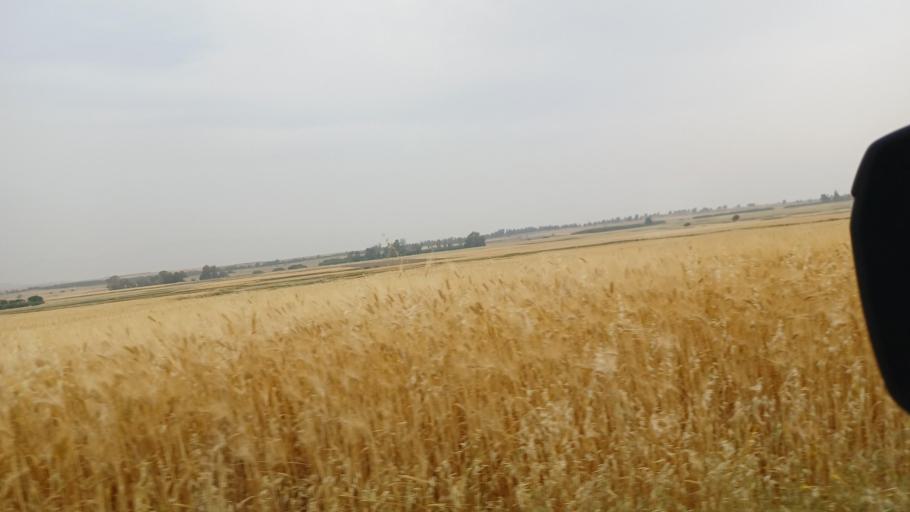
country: CY
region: Lefkosia
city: Mammari
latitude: 35.1729
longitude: 33.2236
